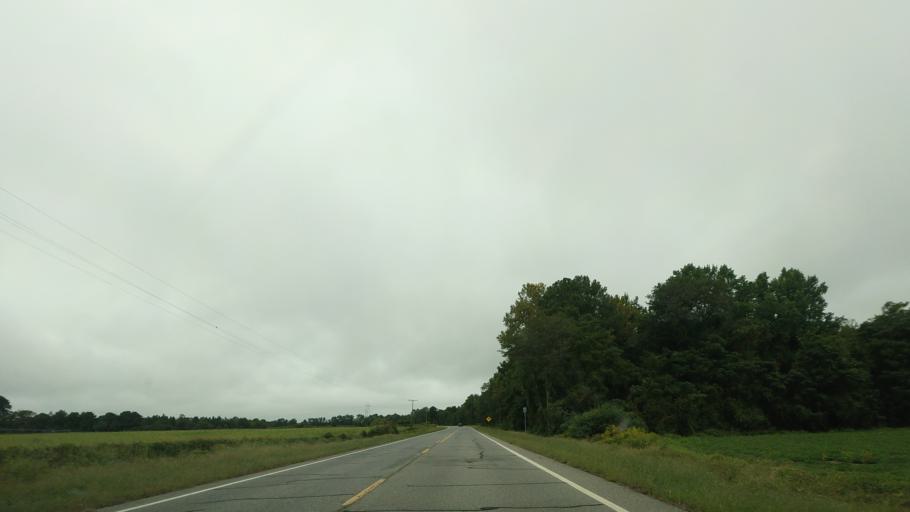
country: US
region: Georgia
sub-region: Irwin County
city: Ocilla
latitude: 31.5313
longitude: -83.2473
